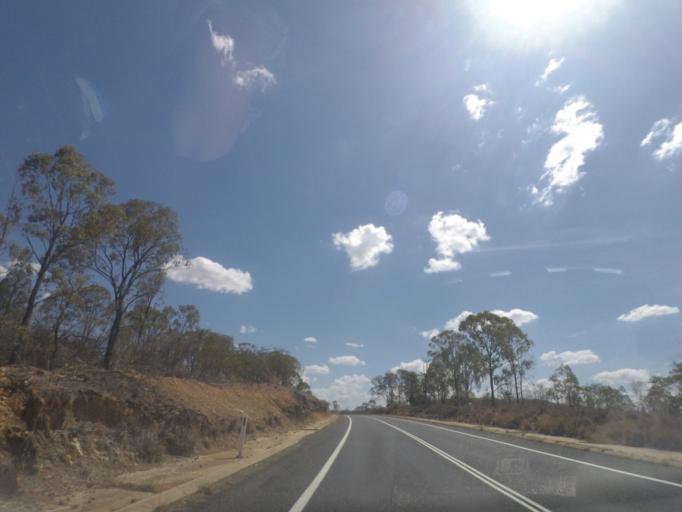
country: AU
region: Queensland
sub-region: Southern Downs
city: Warwick
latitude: -28.2192
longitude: 151.5571
